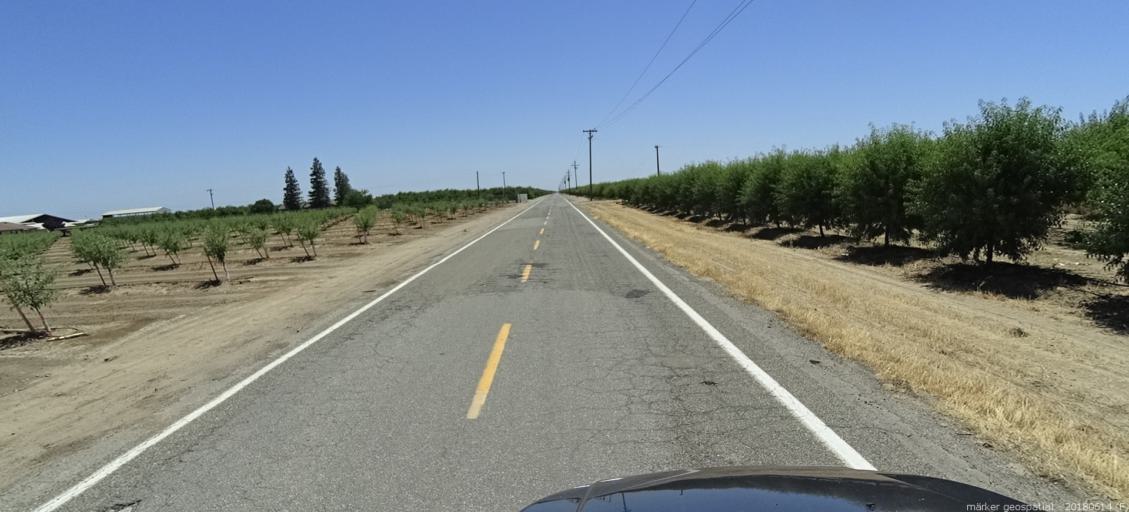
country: US
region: California
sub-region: Madera County
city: Chowchilla
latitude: 37.0400
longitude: -120.2710
